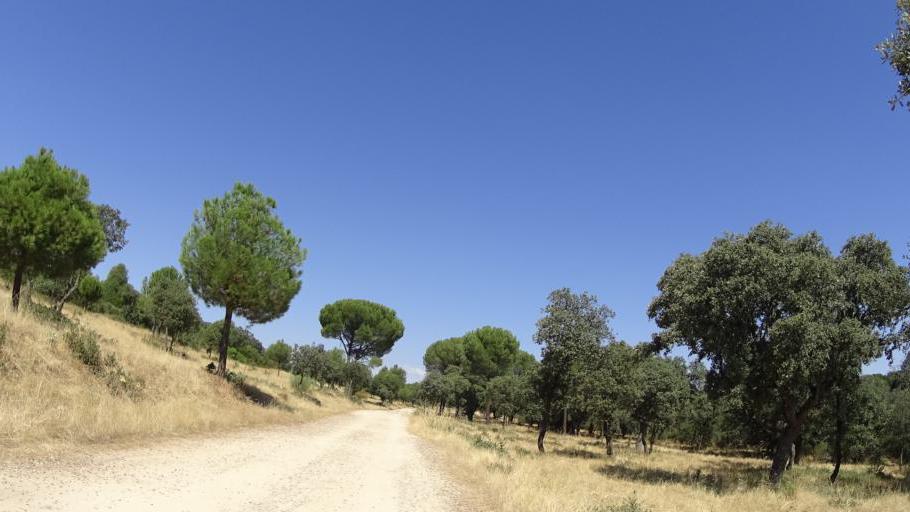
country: ES
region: Madrid
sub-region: Provincia de Madrid
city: Boadilla del Monte
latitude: 40.4277
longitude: -3.8538
